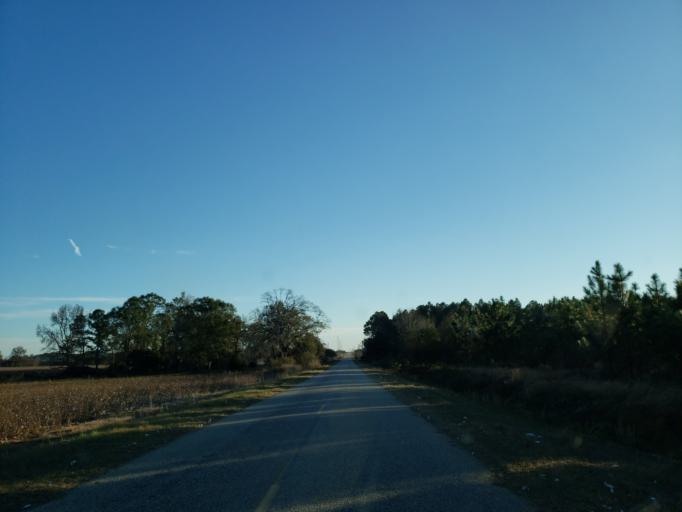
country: US
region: Georgia
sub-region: Dooly County
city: Vienna
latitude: 32.1519
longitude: -83.7608
